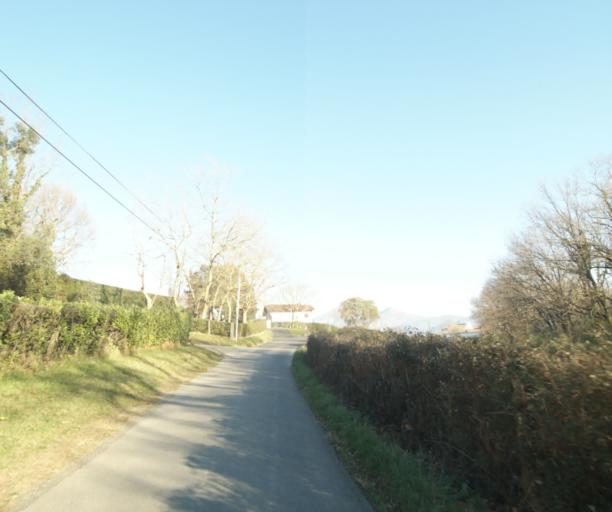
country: FR
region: Aquitaine
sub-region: Departement des Pyrenees-Atlantiques
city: Urrugne
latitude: 43.3469
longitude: -1.7037
